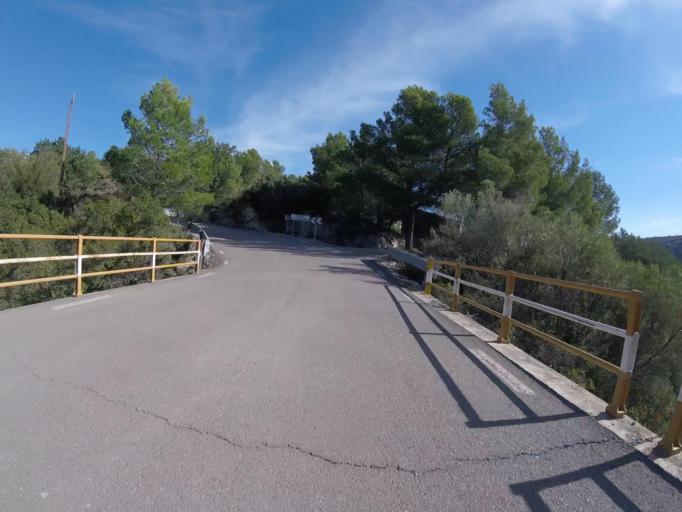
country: ES
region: Valencia
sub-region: Provincia de Castello
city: Sarratella
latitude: 40.2722
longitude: 0.0383
